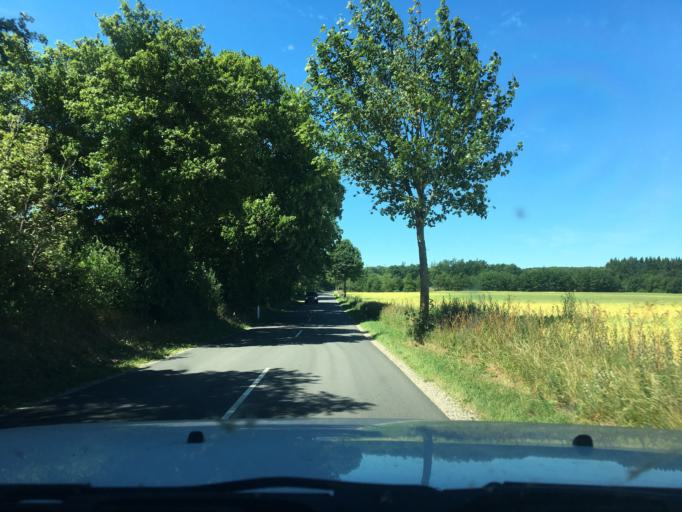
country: DK
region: Central Jutland
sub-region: Syddjurs Kommune
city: Hornslet
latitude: 56.3292
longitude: 10.3452
